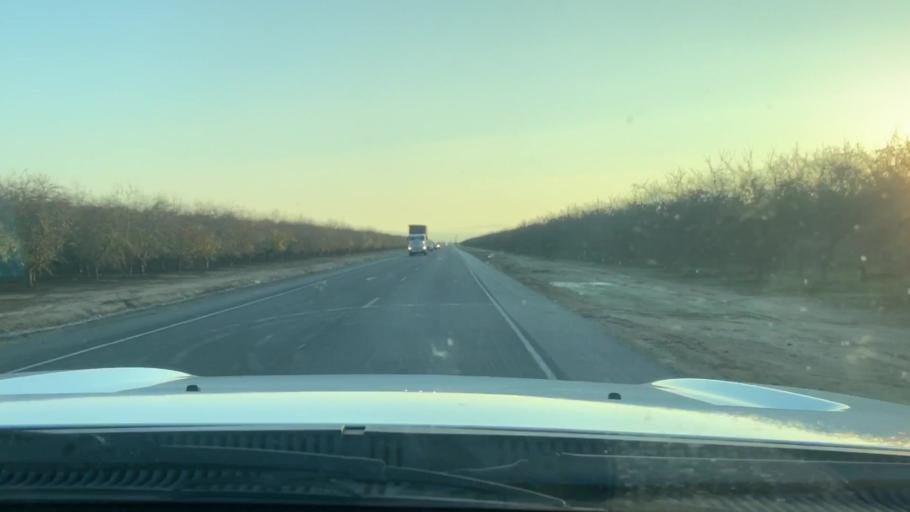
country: US
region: California
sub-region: Kern County
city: Wasco
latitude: 35.5003
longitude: -119.3989
